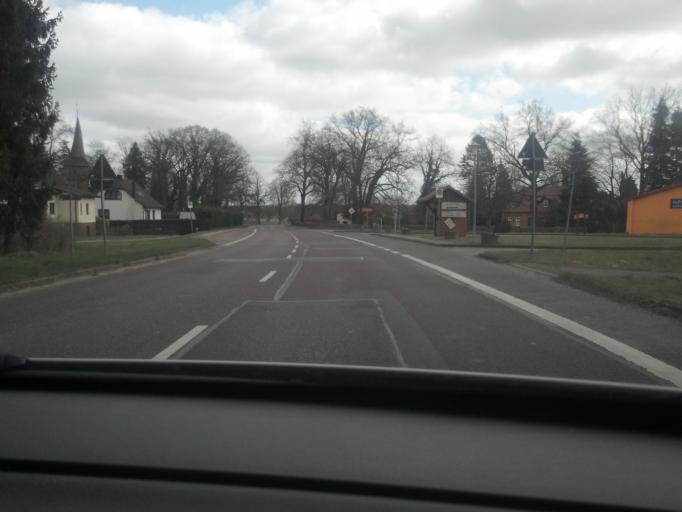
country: DE
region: Mecklenburg-Vorpommern
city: Plau am See
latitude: 53.3791
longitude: 12.3353
